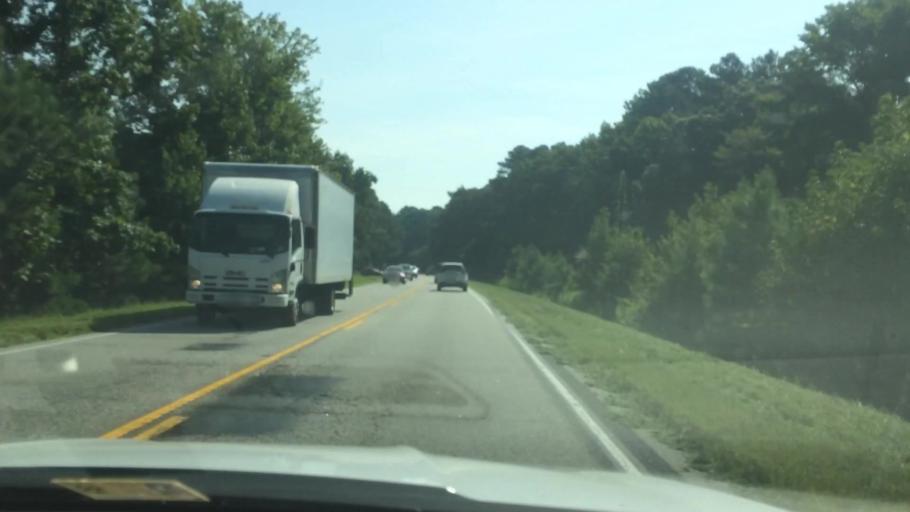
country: US
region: Virginia
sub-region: City of Poquoson
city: Poquoson
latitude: 37.1233
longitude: -76.4172
